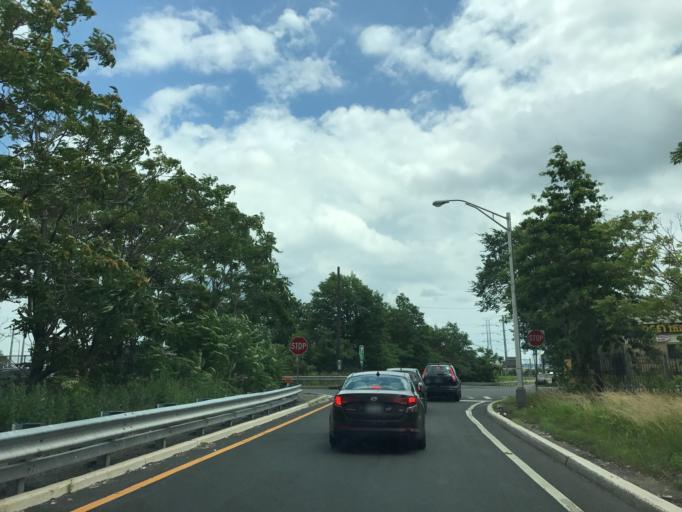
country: US
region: New Jersey
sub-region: Union County
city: Elizabeth
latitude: 40.6427
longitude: -74.2142
